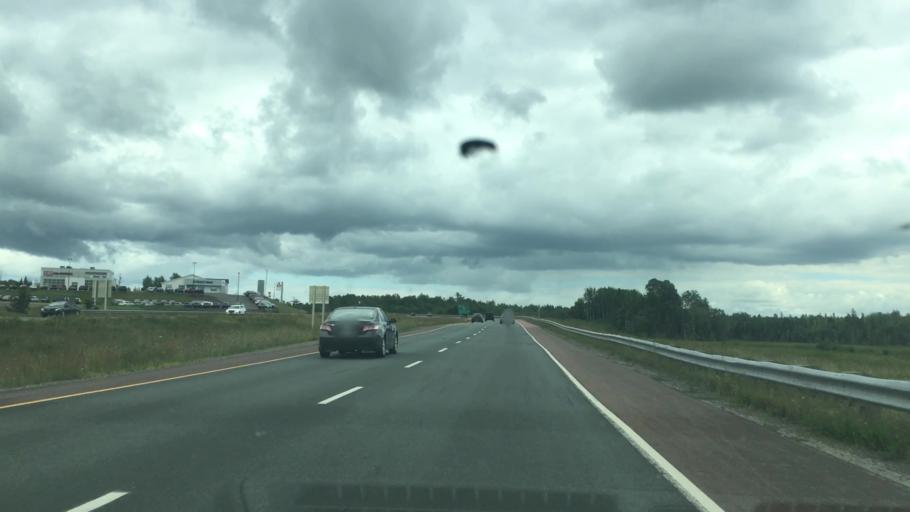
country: CA
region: Nova Scotia
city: Antigonish
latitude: 45.5972
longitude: -62.0358
